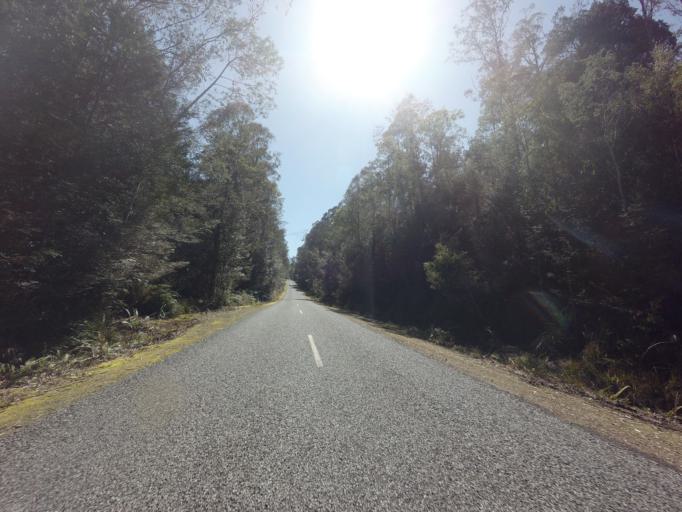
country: AU
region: Tasmania
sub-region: Derwent Valley
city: New Norfolk
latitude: -42.7489
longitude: 146.4129
